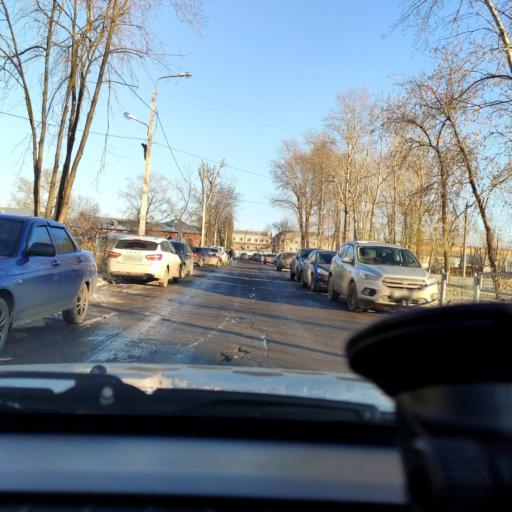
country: RU
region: Perm
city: Perm
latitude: 57.9731
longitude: 56.2431
